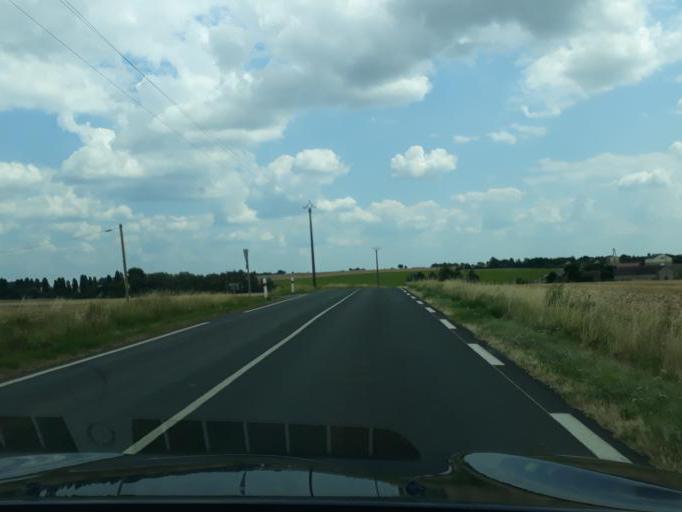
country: FR
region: Centre
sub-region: Departement du Cher
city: Baugy
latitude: 47.0101
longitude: 2.7343
